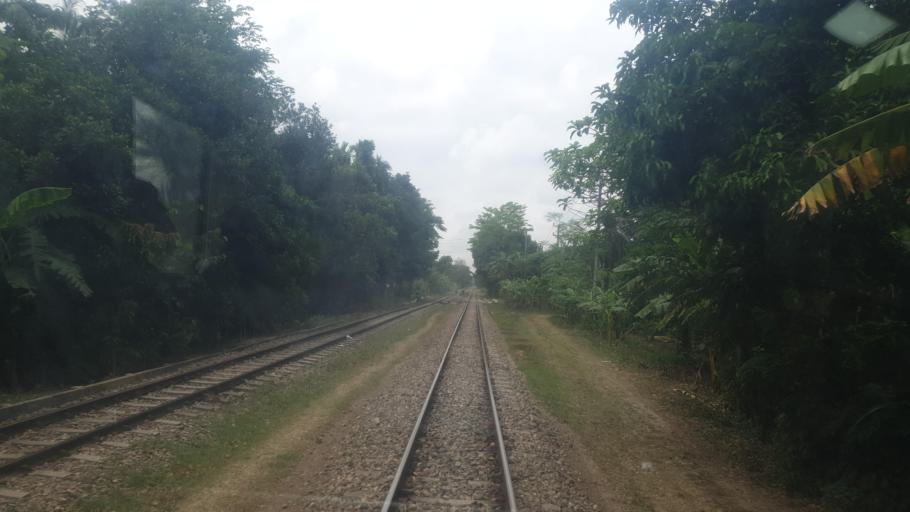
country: BD
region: Chittagong
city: Fatikchari
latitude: 22.6499
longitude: 91.6477
